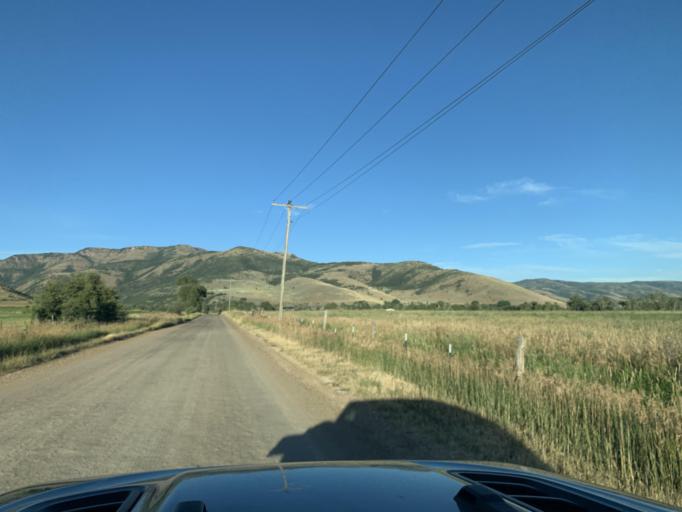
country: US
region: Utah
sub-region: Weber County
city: Wolf Creek
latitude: 41.2931
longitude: -111.7701
